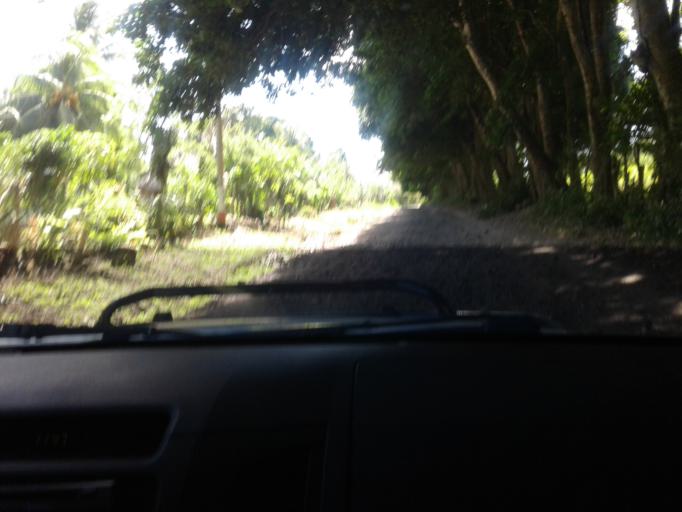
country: NI
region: Rivas
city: Altagracia
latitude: 11.4622
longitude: -85.5605
